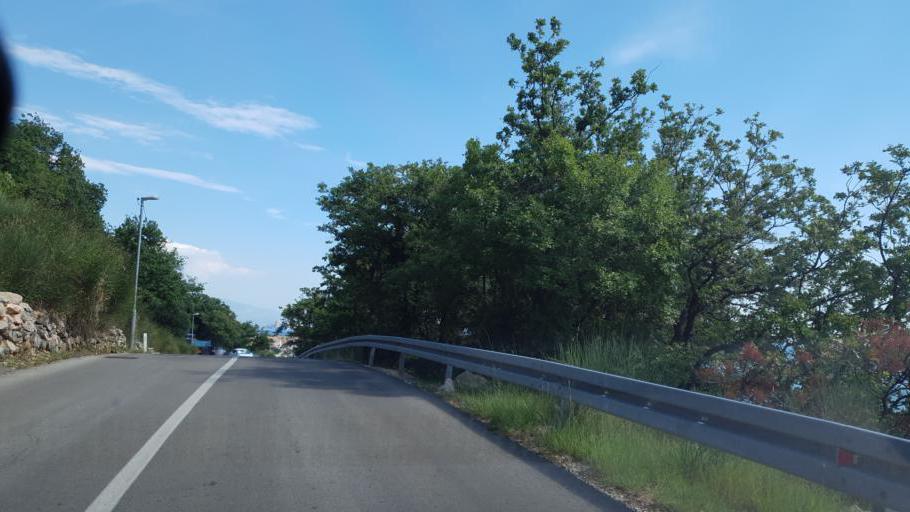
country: HR
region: Primorsko-Goranska
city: Punat
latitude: 44.9641
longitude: 14.6804
